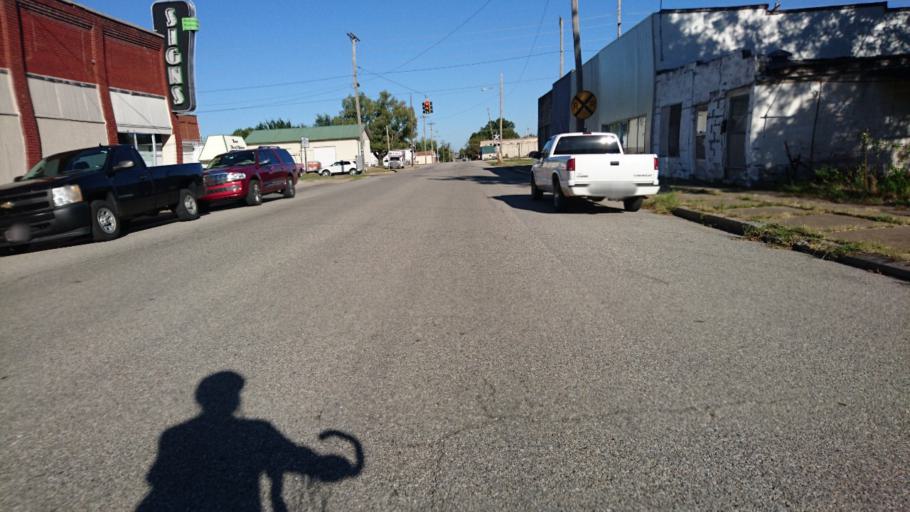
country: US
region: Oklahoma
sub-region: Ottawa County
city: Miami
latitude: 36.8747
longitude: -94.8742
